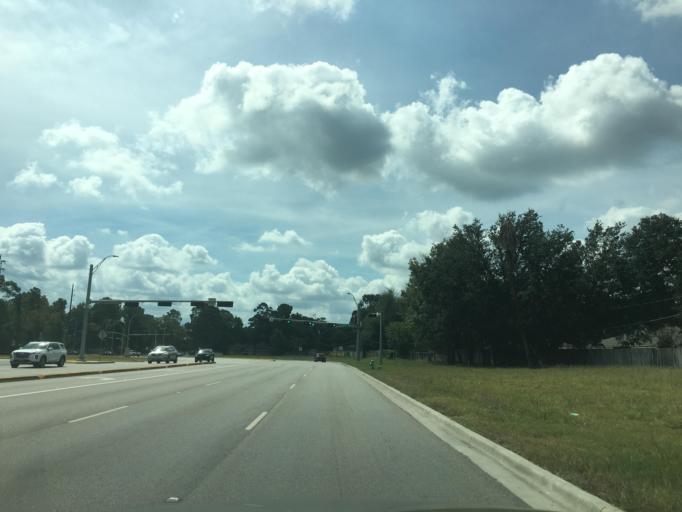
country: US
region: Texas
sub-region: Harris County
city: Spring
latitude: 30.1186
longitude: -95.3975
